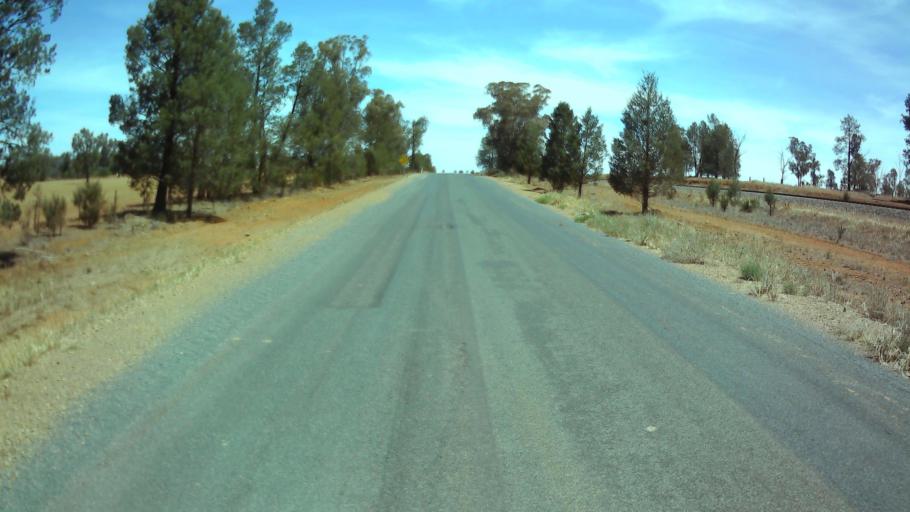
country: AU
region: New South Wales
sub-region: Weddin
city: Grenfell
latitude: -33.7708
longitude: 147.7569
